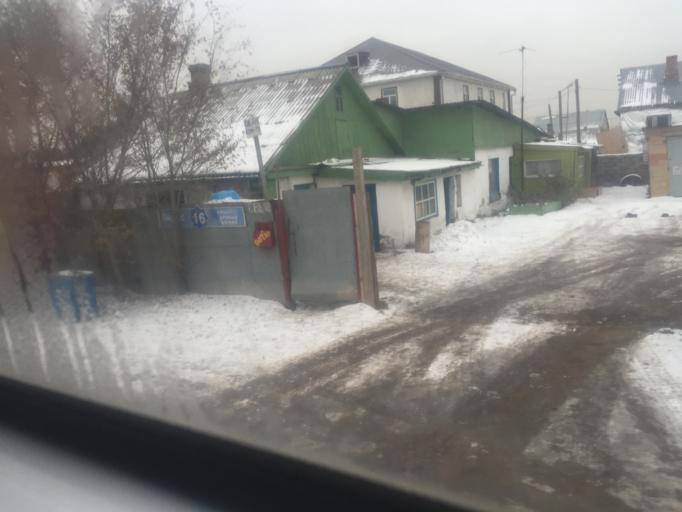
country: KZ
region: Astana Qalasy
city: Astana
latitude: 51.2077
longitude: 71.4083
